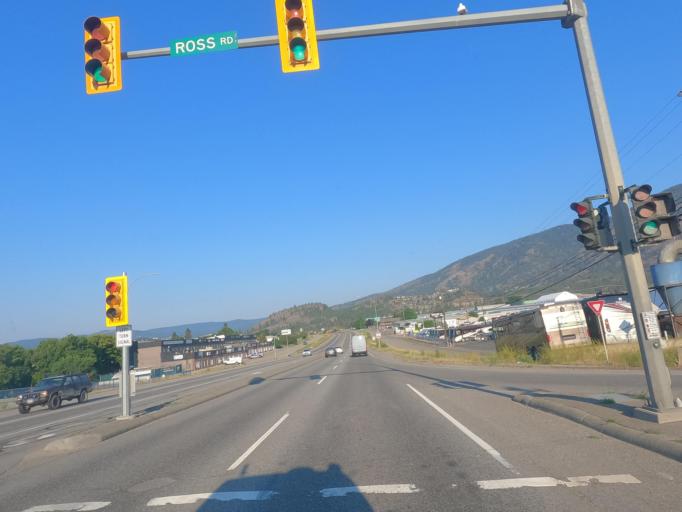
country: CA
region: British Columbia
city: West Kelowna
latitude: 49.8628
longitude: -119.5763
